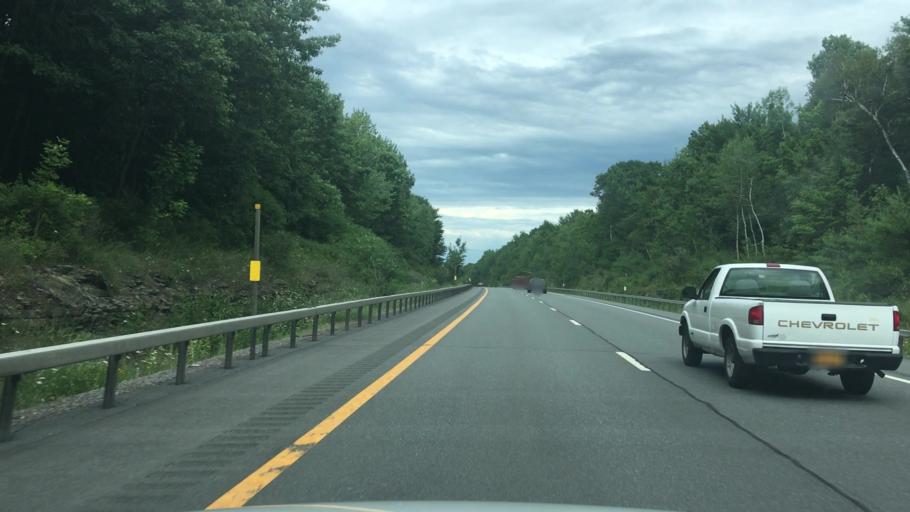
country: US
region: New York
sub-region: Schoharie County
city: Schoharie
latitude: 42.7240
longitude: -74.2233
